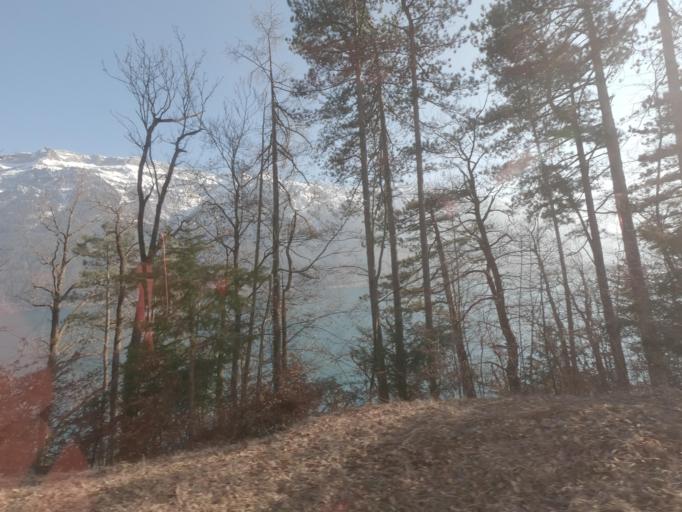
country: CH
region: Bern
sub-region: Interlaken-Oberhasli District
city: Ringgenberg
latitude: 46.7053
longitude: 7.9061
